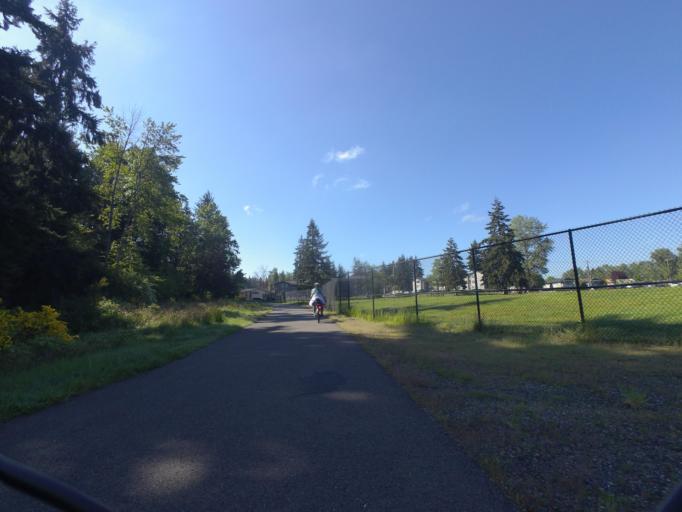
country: US
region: Washington
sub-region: Pierce County
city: Waller
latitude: 47.2074
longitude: -122.4032
